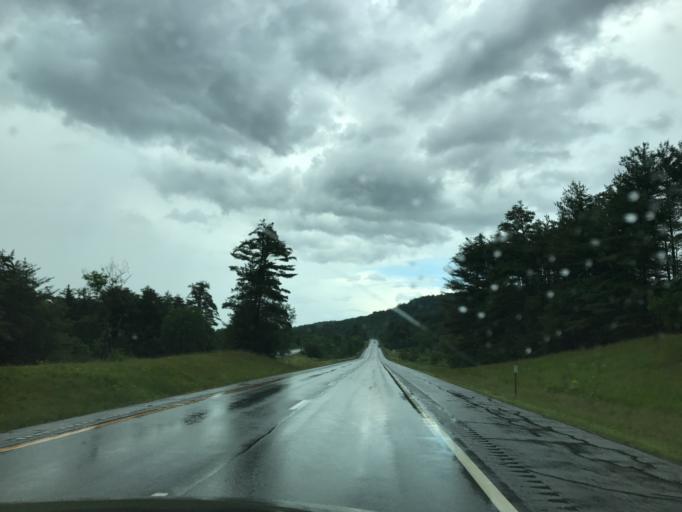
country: US
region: New York
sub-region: Warren County
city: Warrensburg
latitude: 43.4950
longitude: -73.7497
